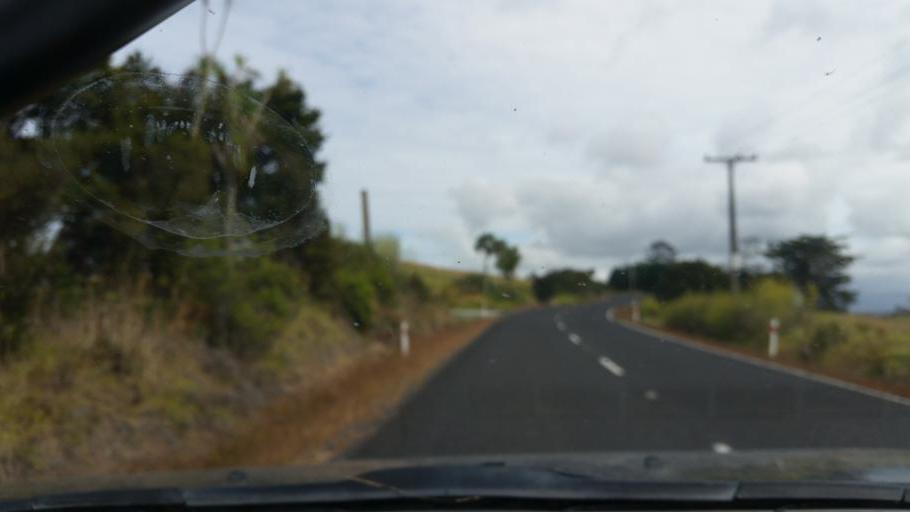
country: NZ
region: Northland
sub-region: Kaipara District
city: Dargaville
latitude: -35.9496
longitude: 173.9164
